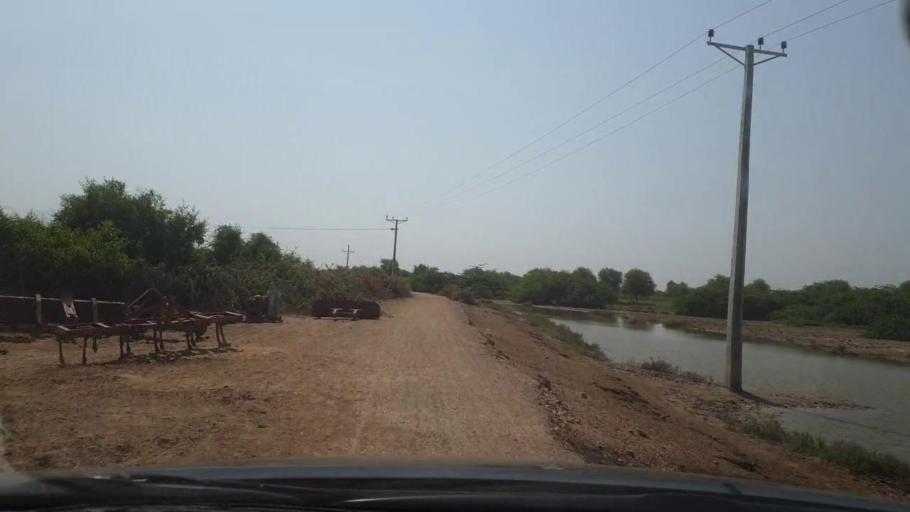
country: PK
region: Sindh
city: Tando Bago
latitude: 24.8005
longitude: 69.1554
